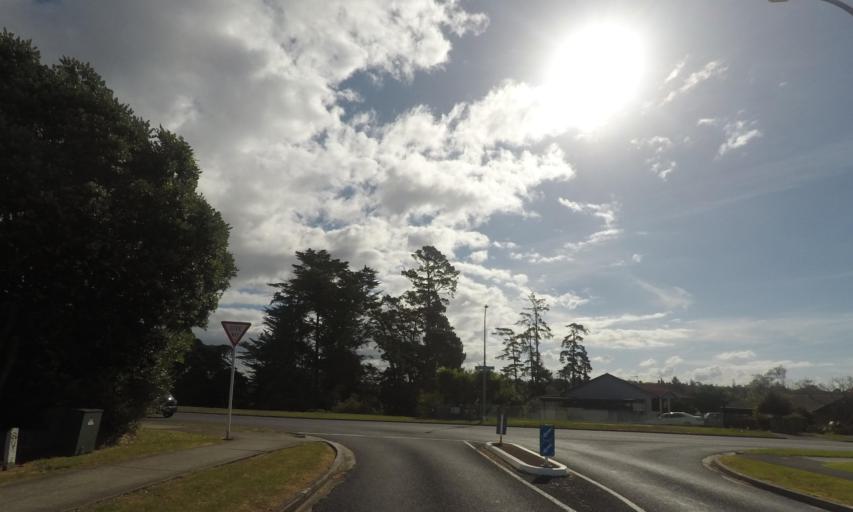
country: NZ
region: Auckland
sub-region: Auckland
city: Pakuranga
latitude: -36.9229
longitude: 174.8963
